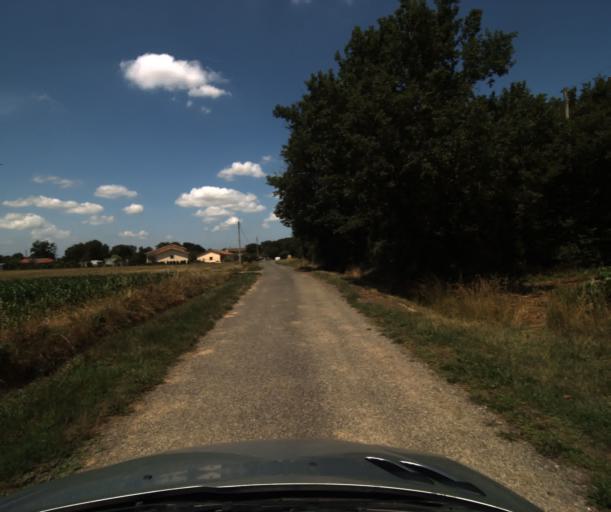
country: FR
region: Midi-Pyrenees
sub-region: Departement de la Haute-Garonne
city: Saint-Lys
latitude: 43.4734
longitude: 1.1928
